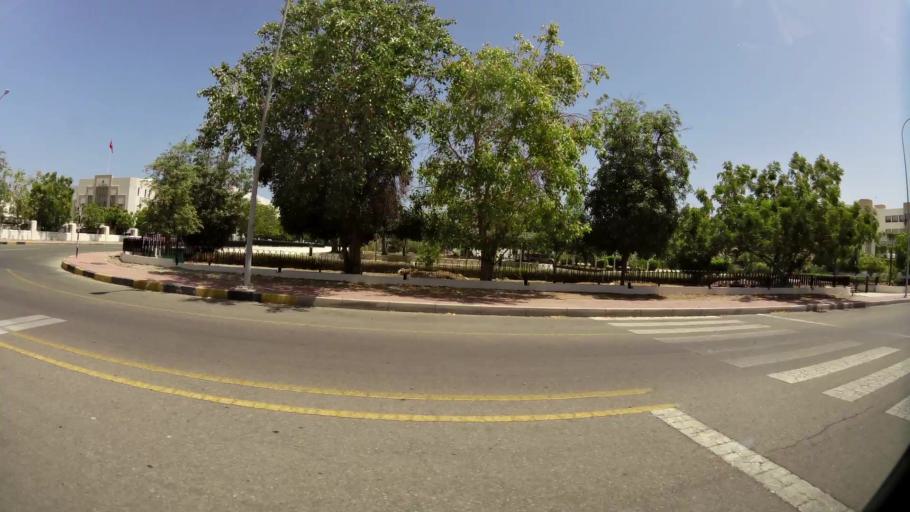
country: OM
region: Muhafazat Masqat
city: Bawshar
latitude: 23.5981
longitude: 58.4357
